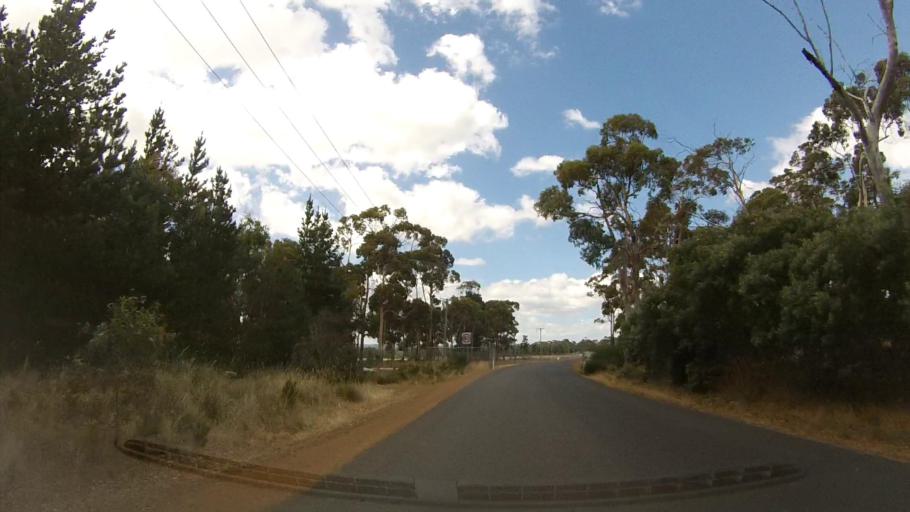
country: AU
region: Tasmania
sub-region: Clarence
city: Seven Mile Beach
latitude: -42.8488
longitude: 147.5218
